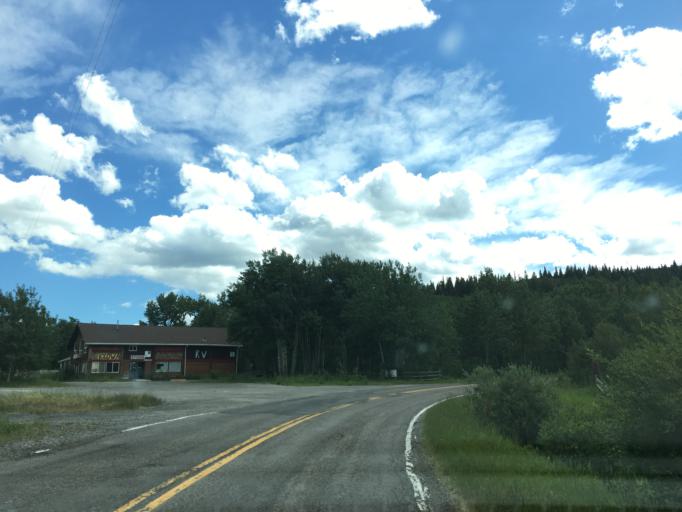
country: US
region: Montana
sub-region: Glacier County
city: South Browning
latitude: 48.5479
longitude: -113.2710
